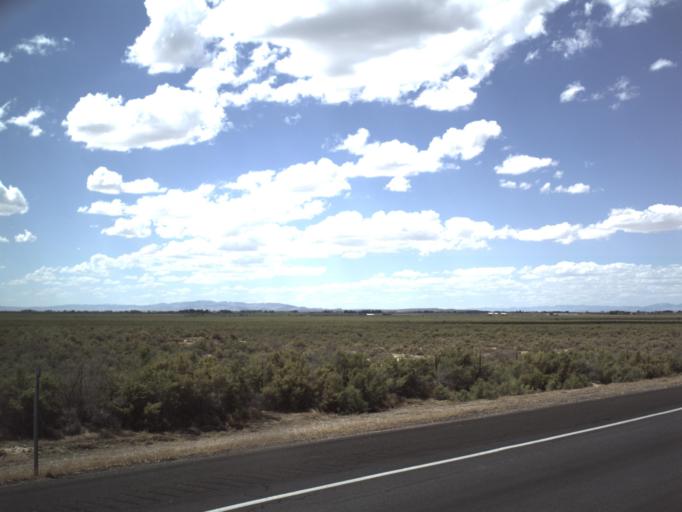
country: US
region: Utah
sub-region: Millard County
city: Delta
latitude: 39.3533
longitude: -112.5024
